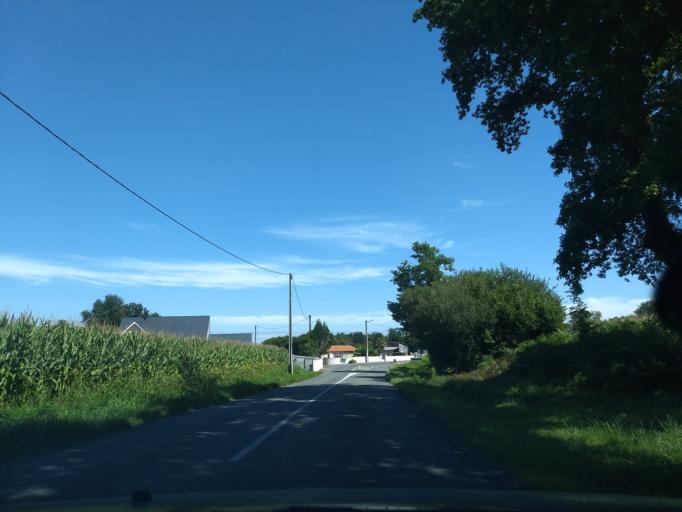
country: FR
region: Aquitaine
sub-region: Departement des Pyrenees-Atlantiques
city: Soumoulou
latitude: 43.2808
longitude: -0.1785
